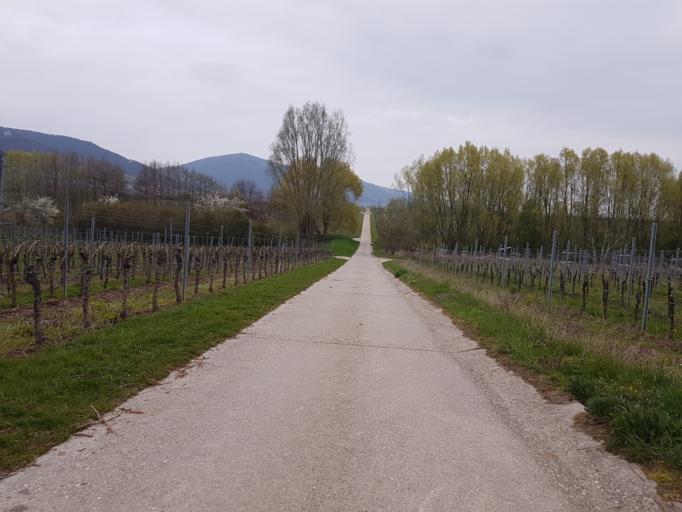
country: DE
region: Rheinland-Pfalz
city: Burrweiler
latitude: 49.2356
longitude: 8.0806
